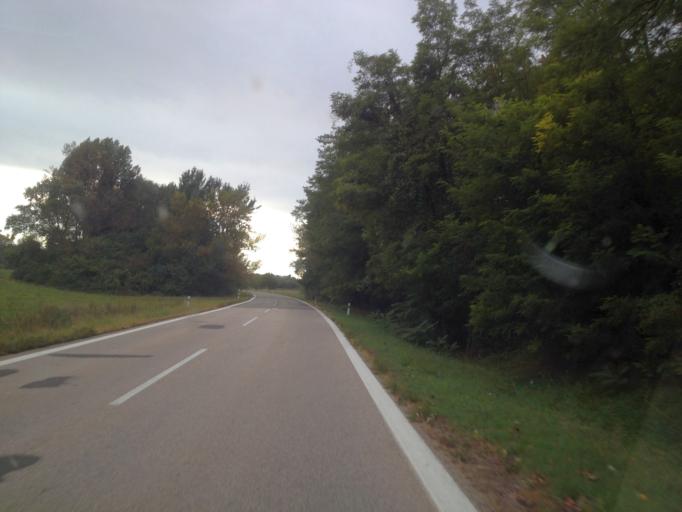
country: HU
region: Komarom-Esztergom
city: Nyergesujfalu
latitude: 47.7727
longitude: 18.5461
